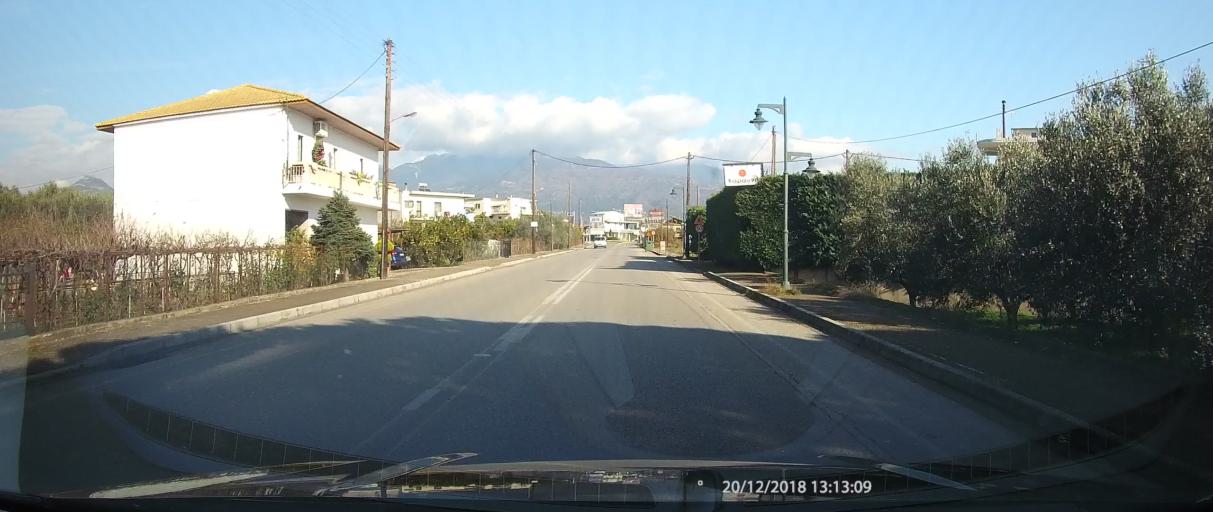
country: GR
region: West Greece
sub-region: Nomos Aitolias kai Akarnanias
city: Kainouryion
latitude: 38.6019
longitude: 21.4766
